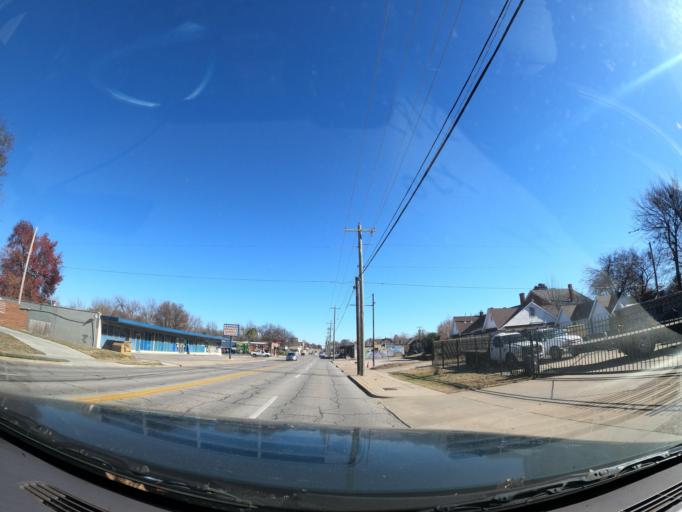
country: US
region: Oklahoma
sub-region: Tulsa County
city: Tulsa
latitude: 36.1405
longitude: -95.9445
